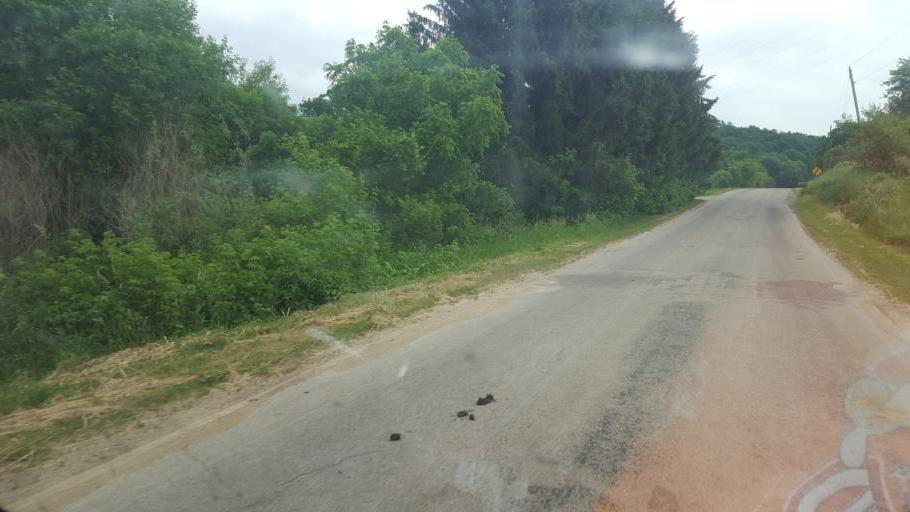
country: US
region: Wisconsin
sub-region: Vernon County
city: Hillsboro
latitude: 43.5943
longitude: -90.3650
